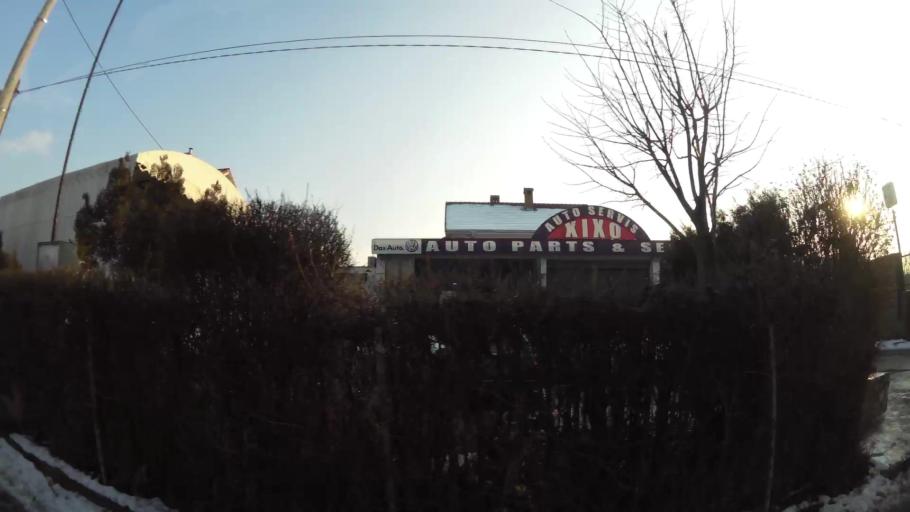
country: MK
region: Aracinovo
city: Arachinovo
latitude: 42.0155
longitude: 21.5250
